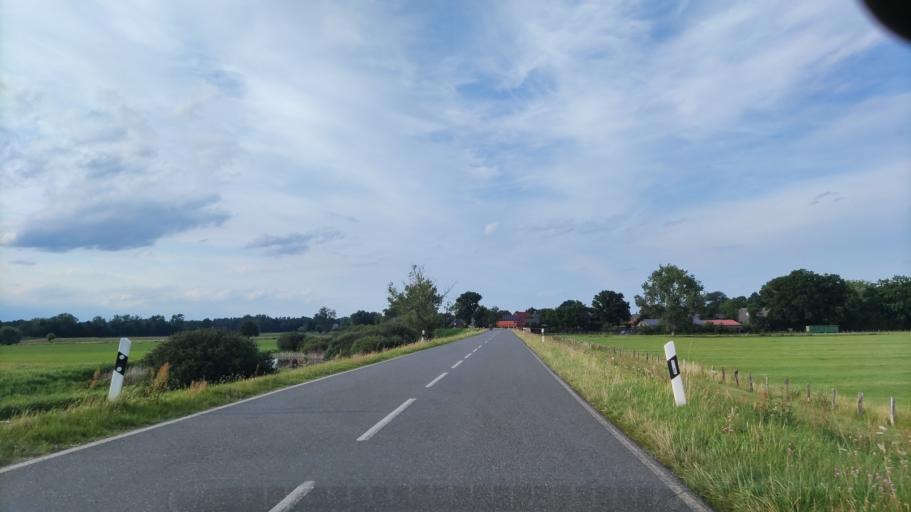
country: DE
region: Lower Saxony
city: Dannenberg
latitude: 53.1327
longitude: 11.1212
